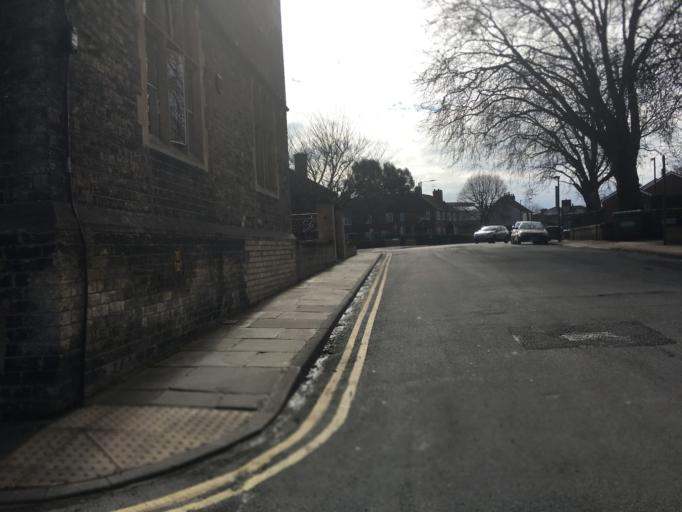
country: GB
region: England
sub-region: City of York
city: York
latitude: 53.9553
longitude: -1.0755
